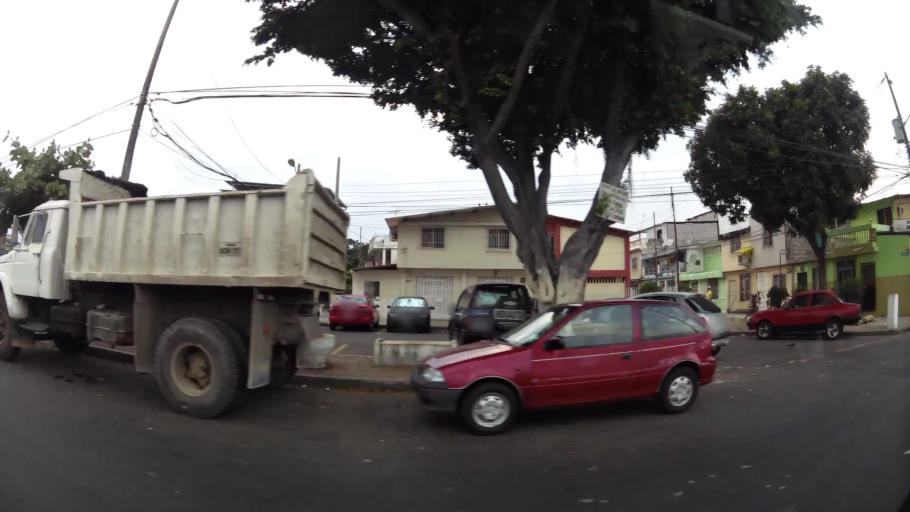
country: EC
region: Guayas
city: Guayaquil
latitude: -2.2376
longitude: -79.8879
